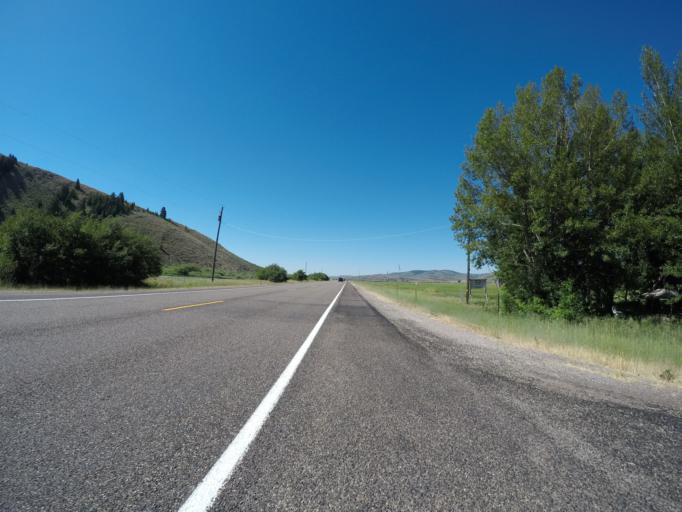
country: US
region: Idaho
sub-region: Bear Lake County
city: Montpelier
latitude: 42.3924
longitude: -111.0518
